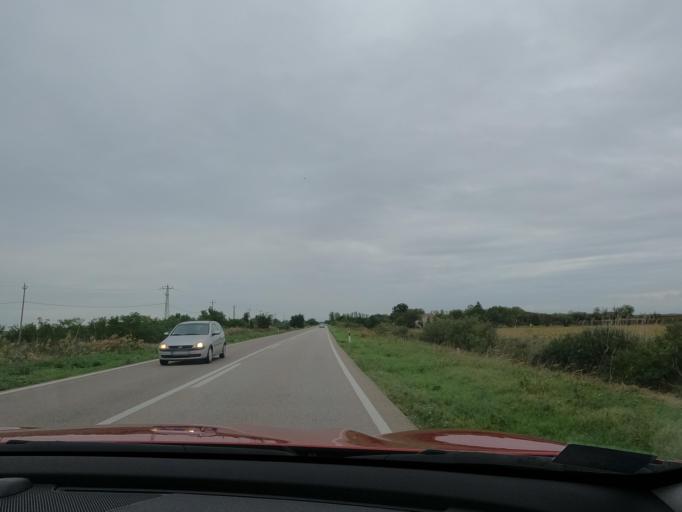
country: RS
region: Autonomna Pokrajina Vojvodina
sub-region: Severnobanatski Okrug
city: Kikinda
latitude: 45.7683
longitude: 20.4236
